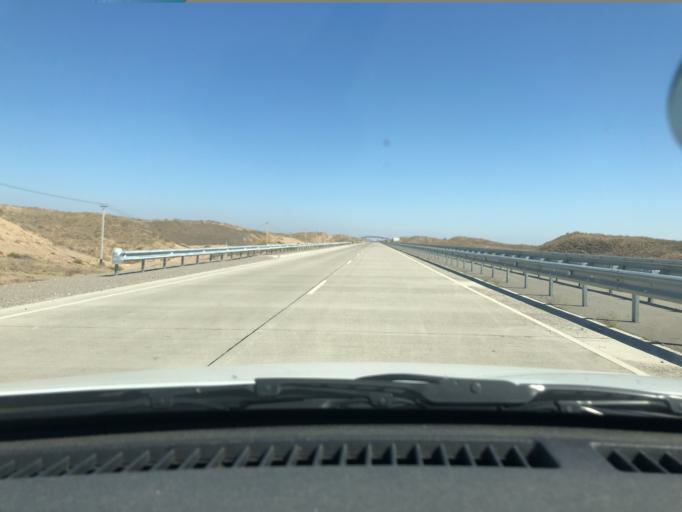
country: KZ
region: Almaty Oblysy
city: Zharkent
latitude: 44.1748
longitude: 80.2969
